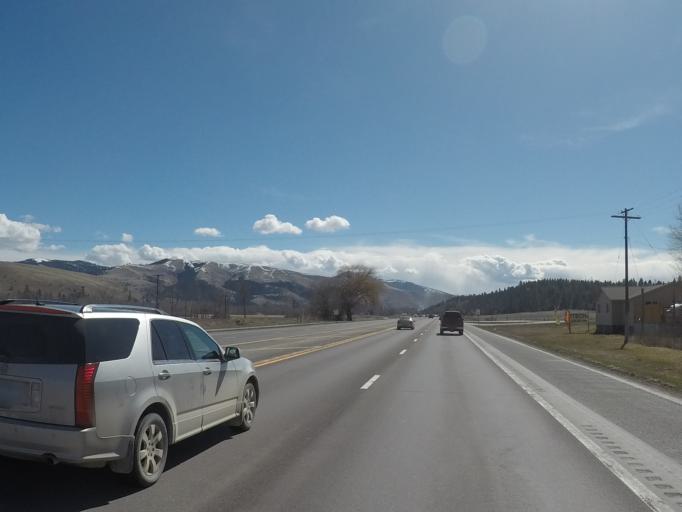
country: US
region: Montana
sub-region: Missoula County
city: Lolo
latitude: 46.7855
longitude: -114.0983
